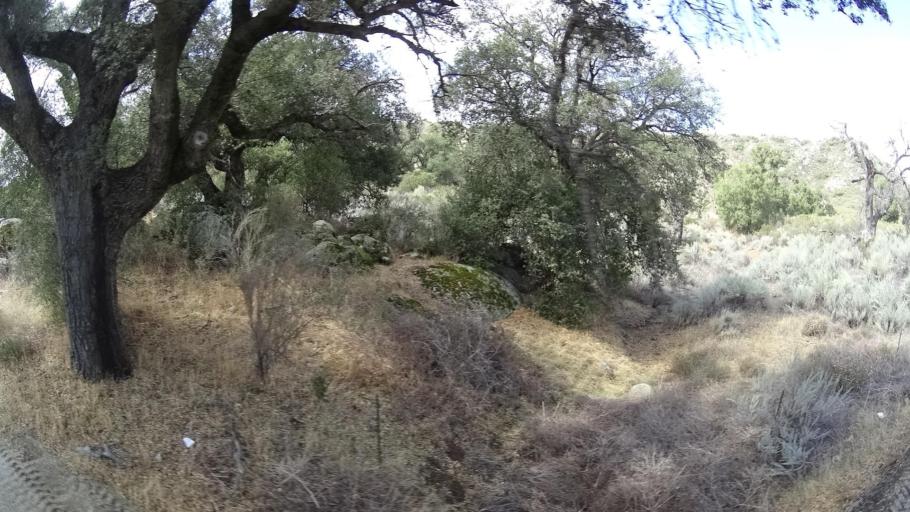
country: US
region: California
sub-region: San Diego County
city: Pine Valley
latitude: 32.7243
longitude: -116.4961
